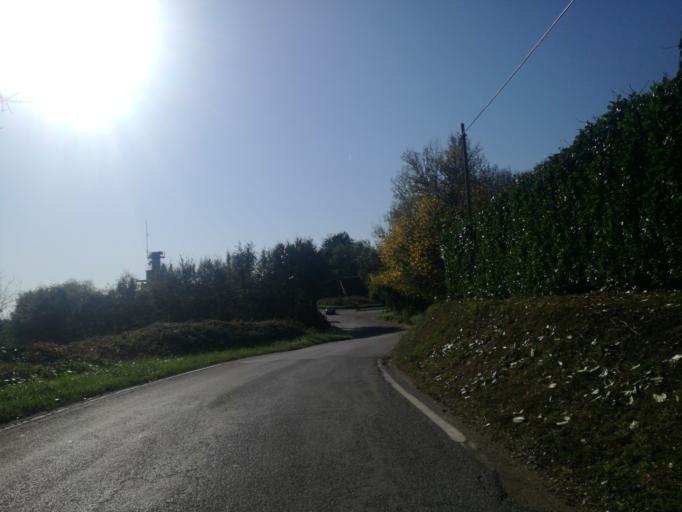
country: IT
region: Lombardy
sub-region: Provincia di Bergamo
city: Suisio
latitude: 45.6443
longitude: 9.4866
